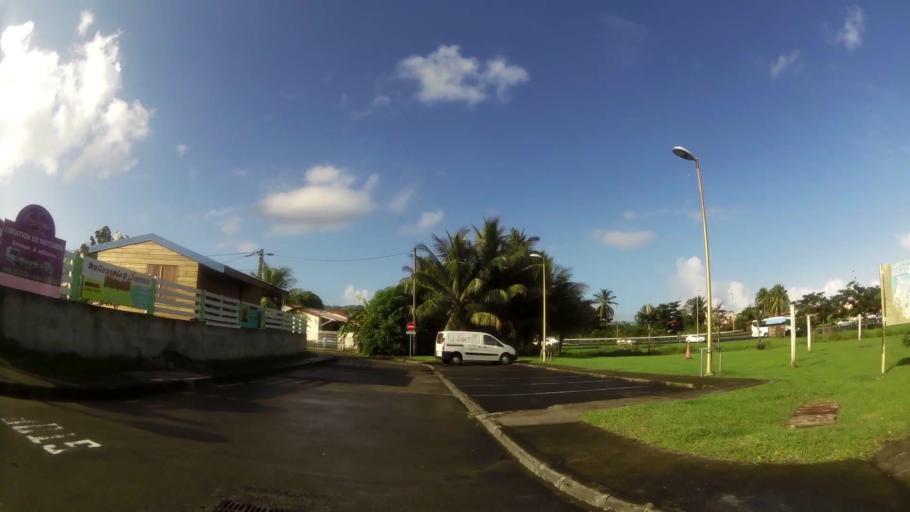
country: MQ
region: Martinique
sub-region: Martinique
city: Ducos
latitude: 14.5320
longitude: -60.9824
